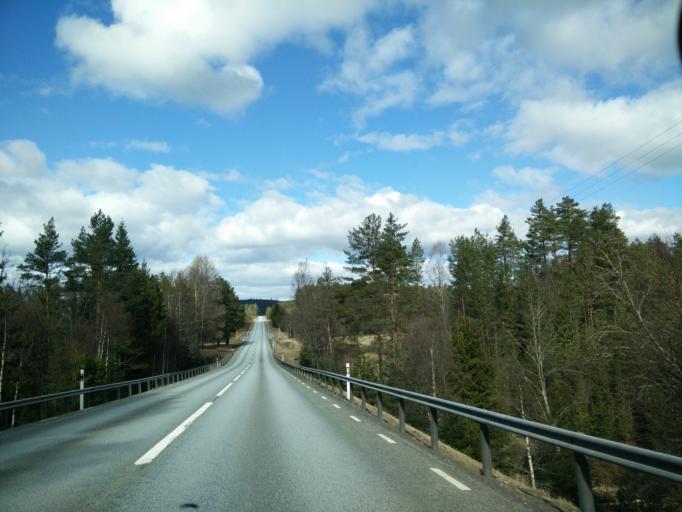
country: SE
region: Vaermland
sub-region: Munkfors Kommun
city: Munkfors
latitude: 59.9308
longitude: 13.5765
